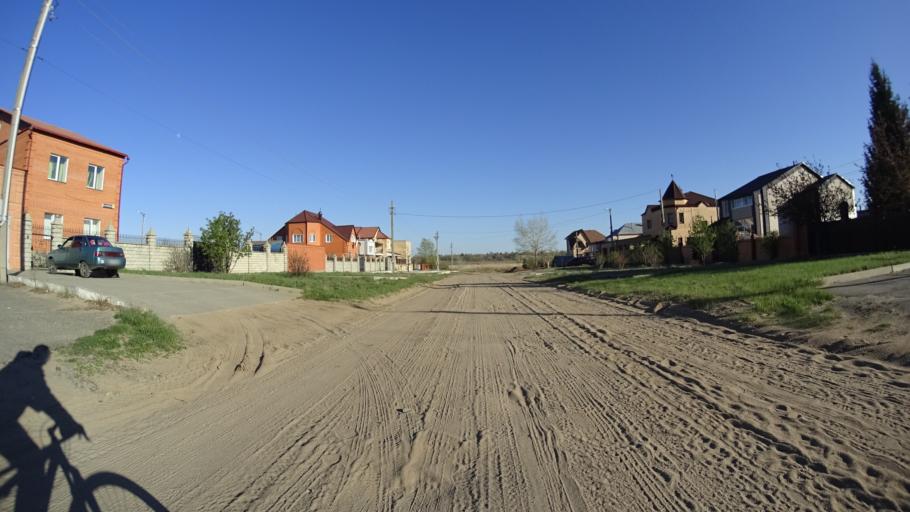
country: RU
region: Chelyabinsk
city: Troitsk
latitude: 54.0704
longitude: 61.5370
